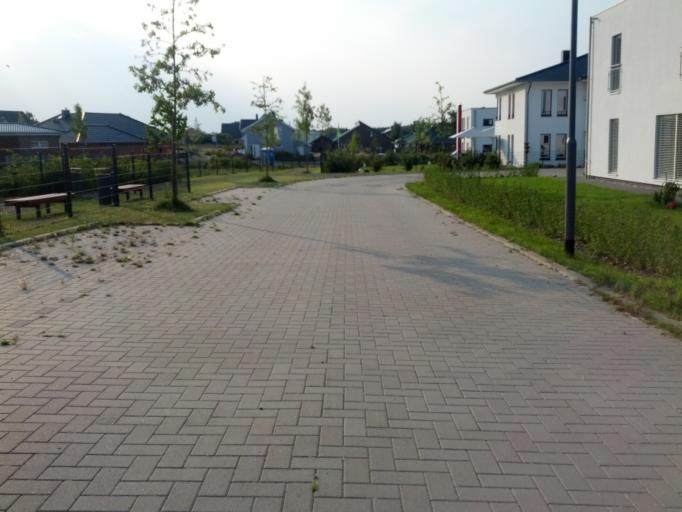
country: DE
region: Mecklenburg-Vorpommern
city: Ostseebad Kuhlungsborn
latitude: 54.1386
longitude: 11.7561
